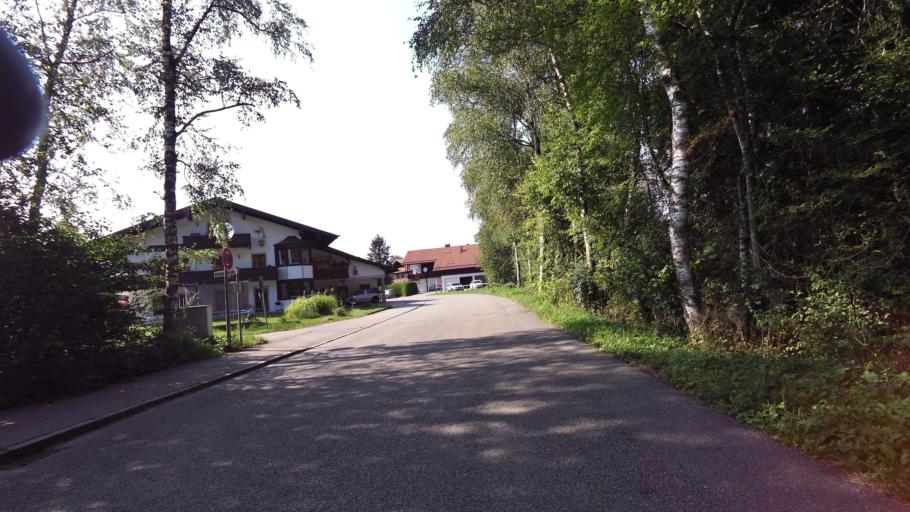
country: DE
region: Bavaria
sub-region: Upper Bavaria
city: Seeon-Seebruck
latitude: 47.9324
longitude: 12.4895
